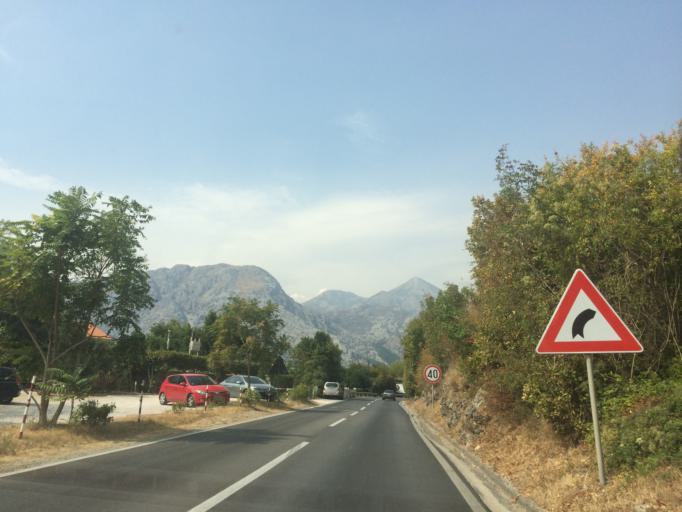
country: ME
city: Dobrota
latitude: 42.4709
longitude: 18.7646
